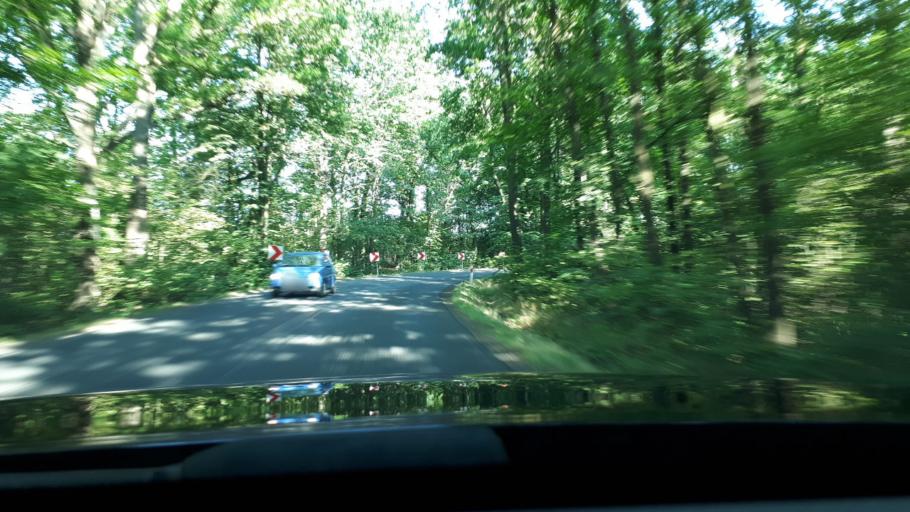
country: PL
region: Lower Silesian Voivodeship
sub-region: Powiat lubanski
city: Pisarzowice
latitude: 51.1540
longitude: 15.2662
